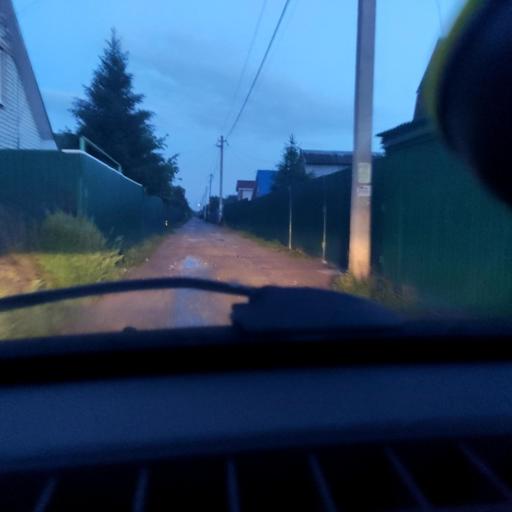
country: RU
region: Samara
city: Tol'yatti
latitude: 53.5932
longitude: 49.3144
